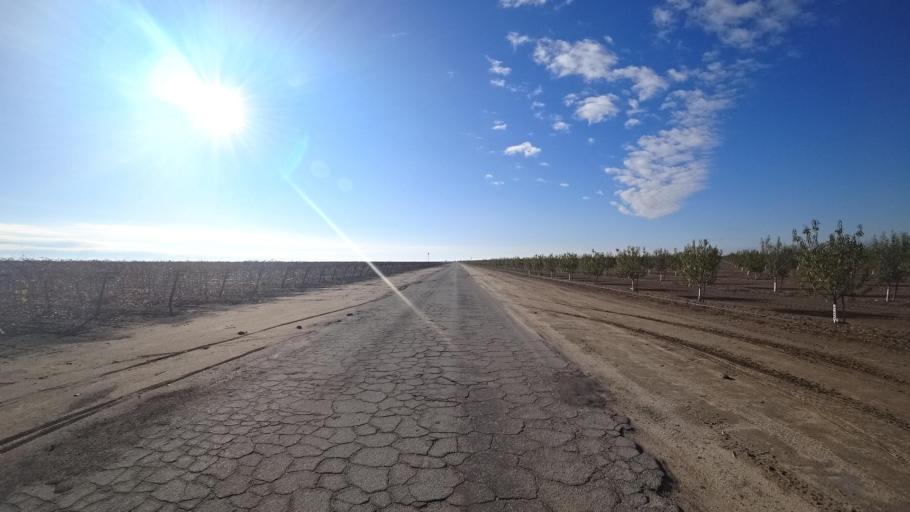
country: US
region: California
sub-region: Kern County
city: Delano
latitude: 35.7171
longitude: -119.2941
